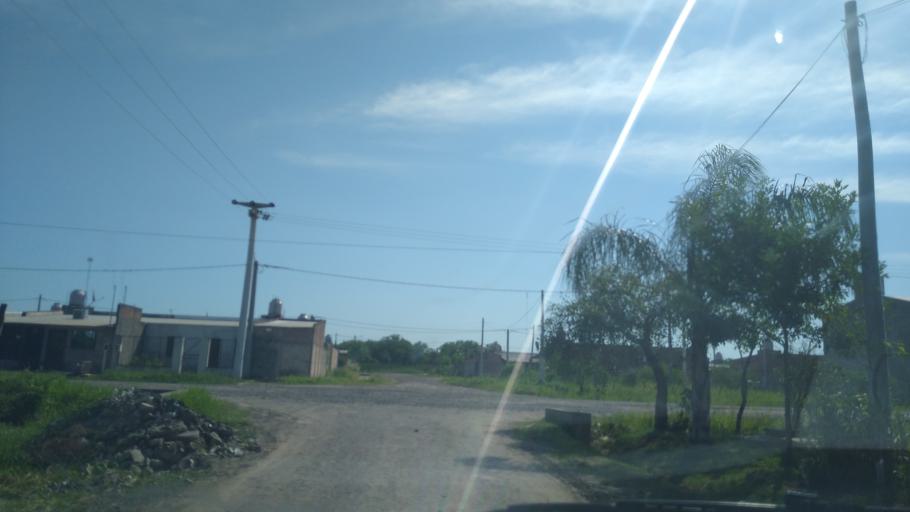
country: AR
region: Chaco
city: Puerto Vilelas
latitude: -27.4963
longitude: -58.9639
